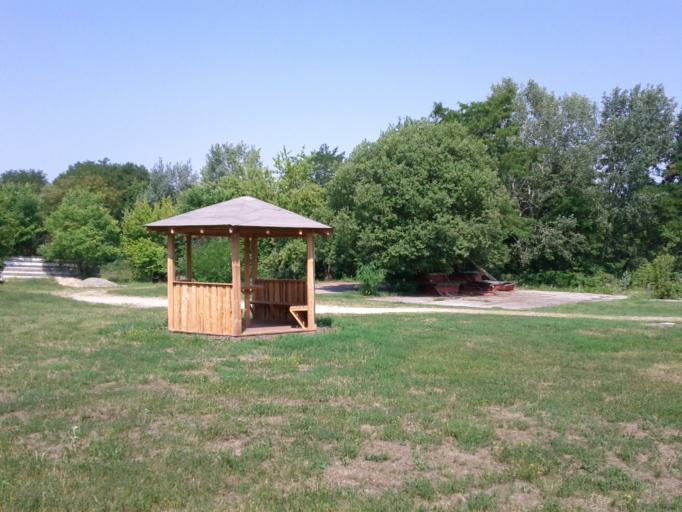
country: DE
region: Brandenburg
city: Woltersdorf
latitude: 52.4805
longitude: 13.7851
